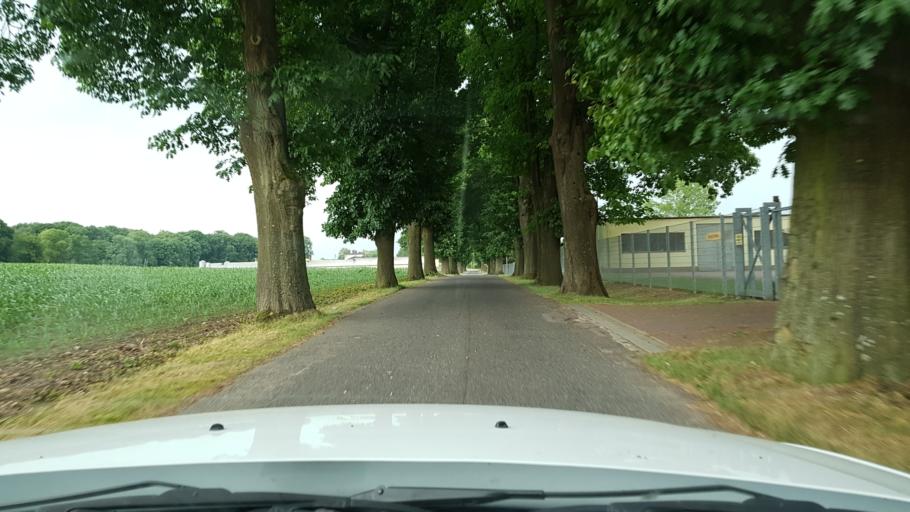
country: PL
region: West Pomeranian Voivodeship
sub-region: Powiat lobeski
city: Lobez
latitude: 53.6774
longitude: 15.6739
